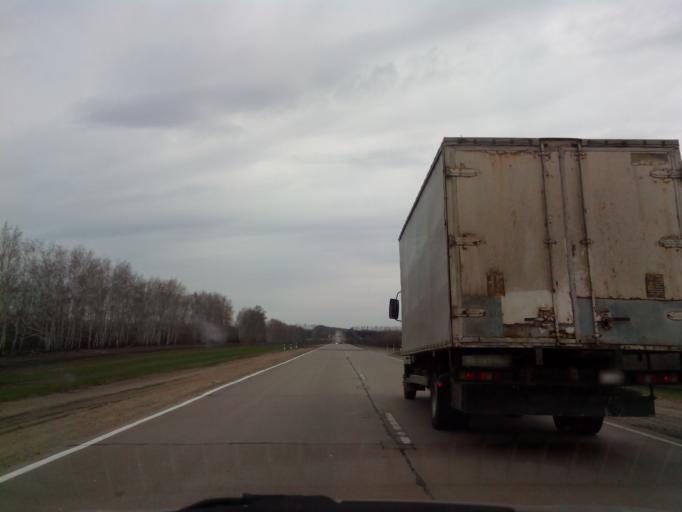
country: RU
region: Tambov
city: Znamenka
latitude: 52.4596
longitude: 41.3674
